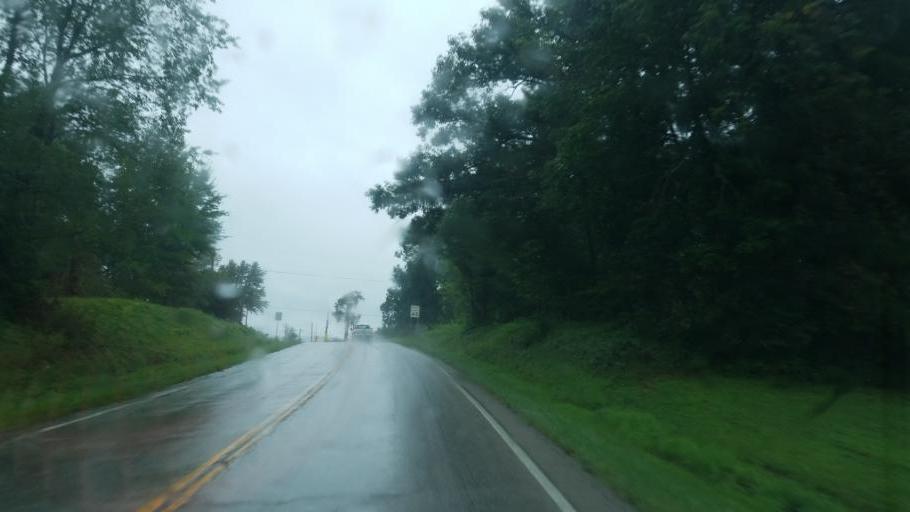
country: US
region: Kentucky
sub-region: Rowan County
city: Morehead
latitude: 38.2125
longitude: -83.4788
